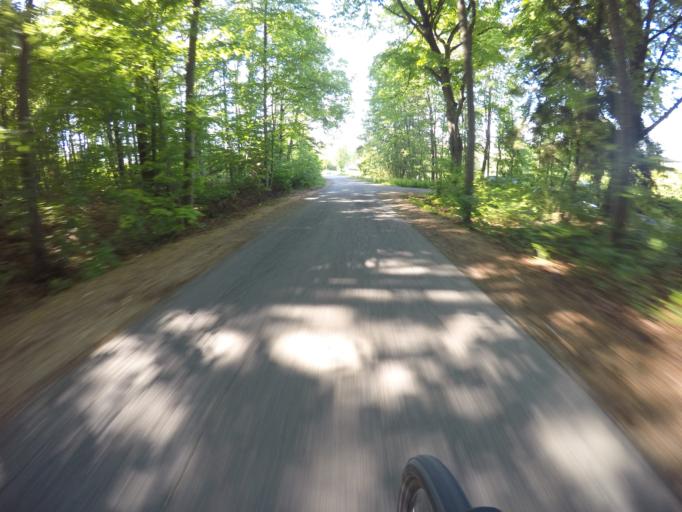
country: DE
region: Baden-Wuerttemberg
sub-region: Karlsruhe Region
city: Wimsheim
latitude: 48.8431
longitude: 8.8296
